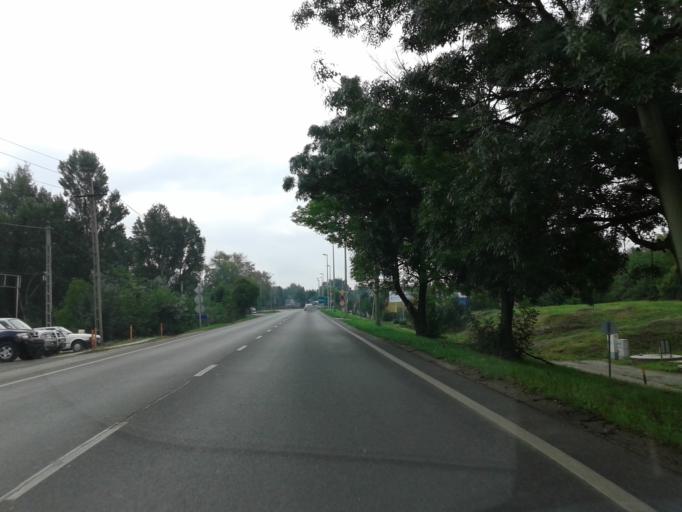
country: HU
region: Csongrad
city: Szeged
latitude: 46.2371
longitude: 20.1698
